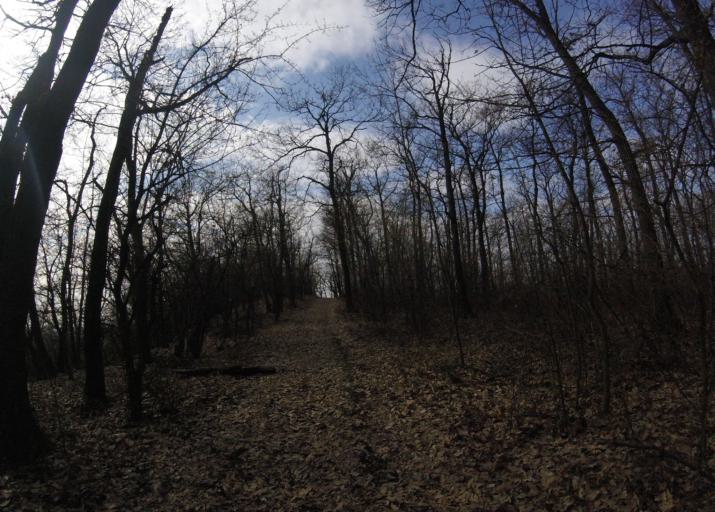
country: HU
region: Heves
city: Belapatfalva
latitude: 48.0049
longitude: 20.3370
